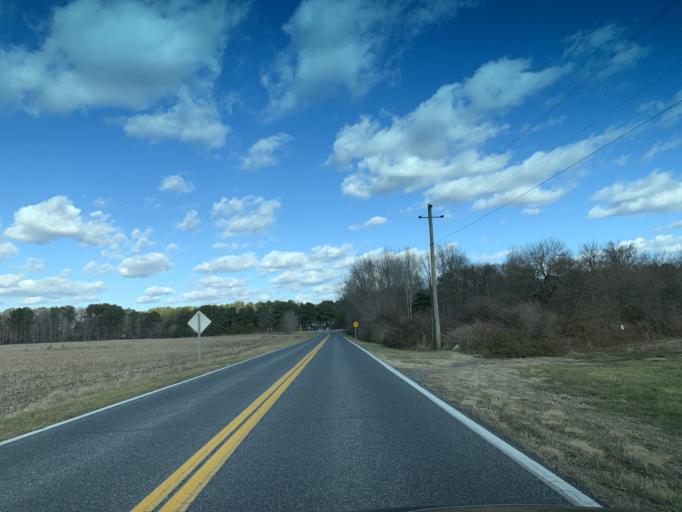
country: US
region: Maryland
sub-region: Worcester County
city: Berlin
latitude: 38.3469
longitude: -75.2174
